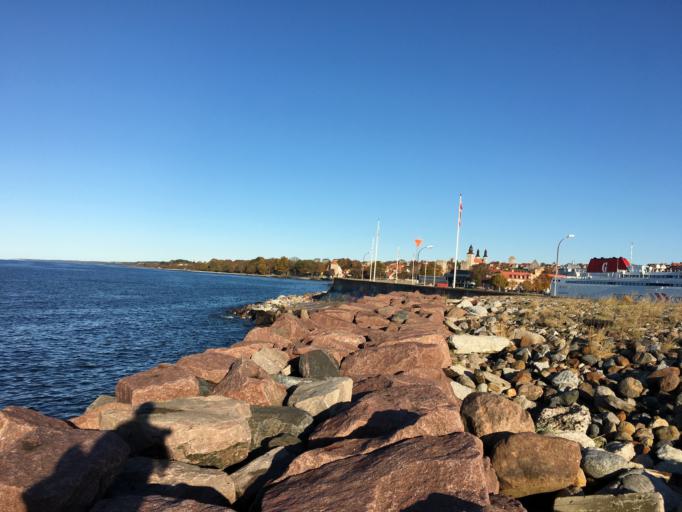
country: SE
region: Gotland
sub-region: Gotland
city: Visby
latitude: 57.6385
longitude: 18.2807
